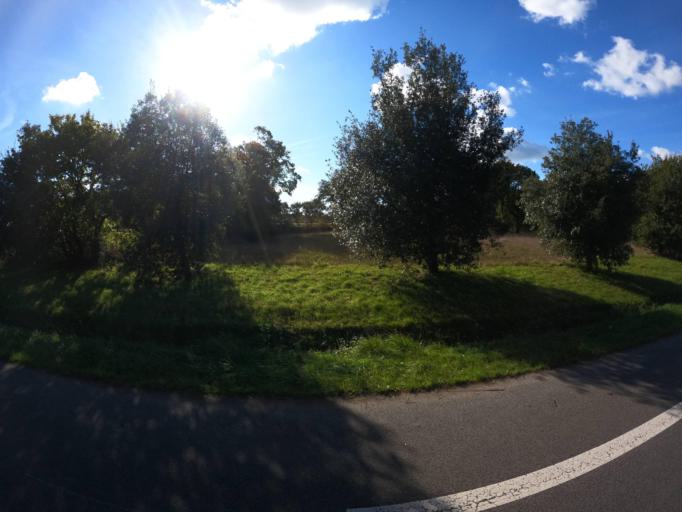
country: FR
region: Pays de la Loire
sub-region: Departement de la Loire-Atlantique
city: La Baule-Escoublac
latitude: 47.2934
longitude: -2.3414
